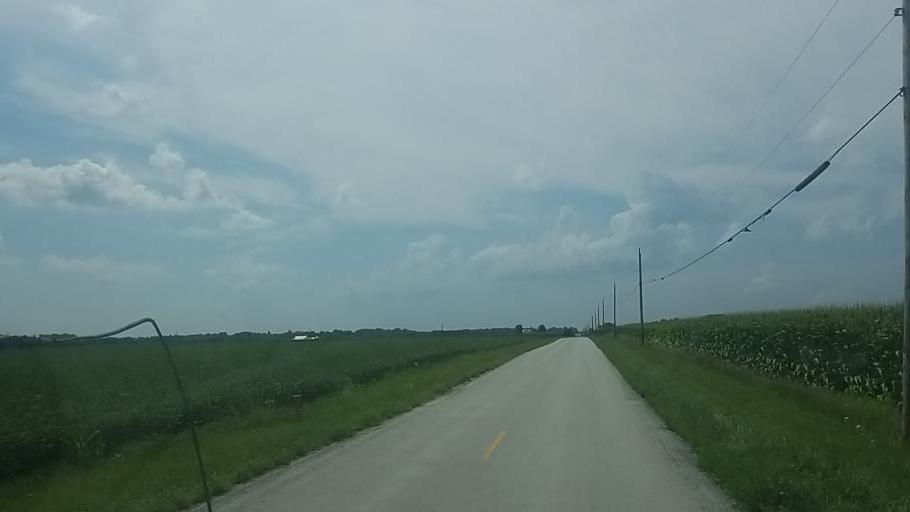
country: US
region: Ohio
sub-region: Hardin County
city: Kenton
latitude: 40.7030
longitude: -83.5883
